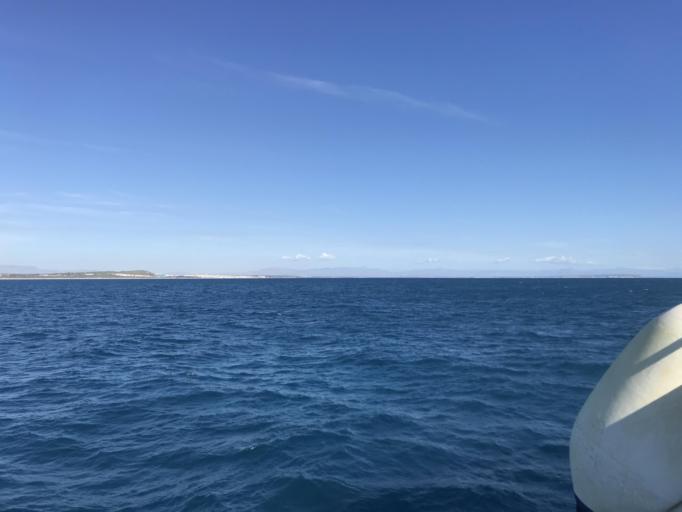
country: ES
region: Valencia
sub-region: Provincia de Alicante
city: Torrevieja
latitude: 38.0135
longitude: -0.6269
